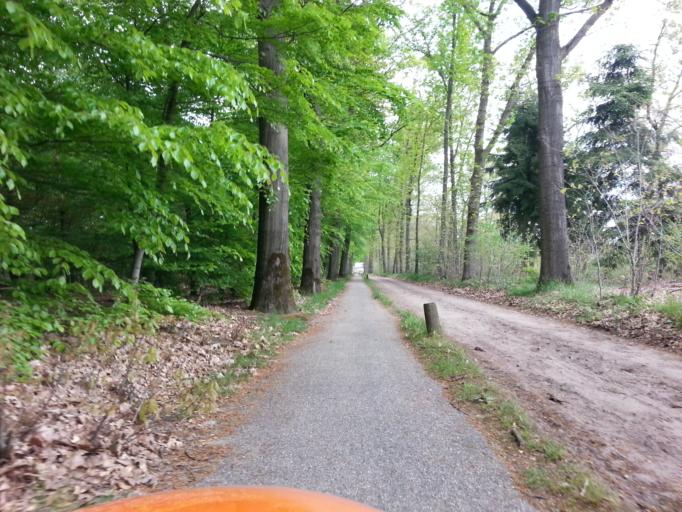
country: NL
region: Gelderland
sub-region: Gemeente Renkum
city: Wolfheze
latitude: 52.0187
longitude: 5.7698
